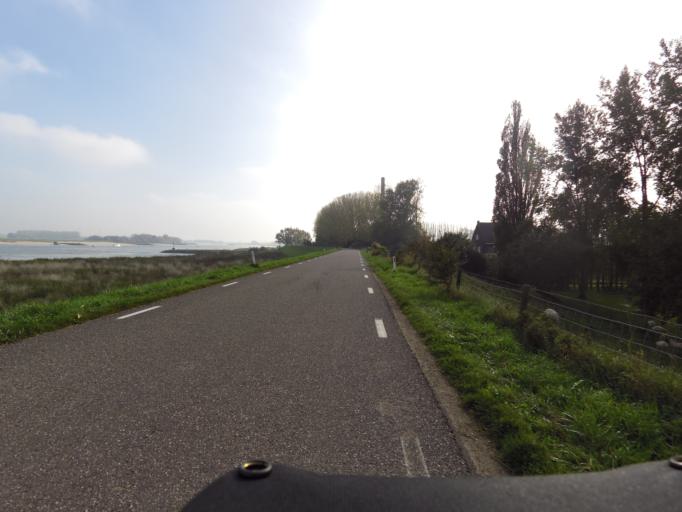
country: NL
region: Gelderland
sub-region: Gemeente Groesbeek
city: Berg en Dal
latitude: 51.8622
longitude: 5.9430
